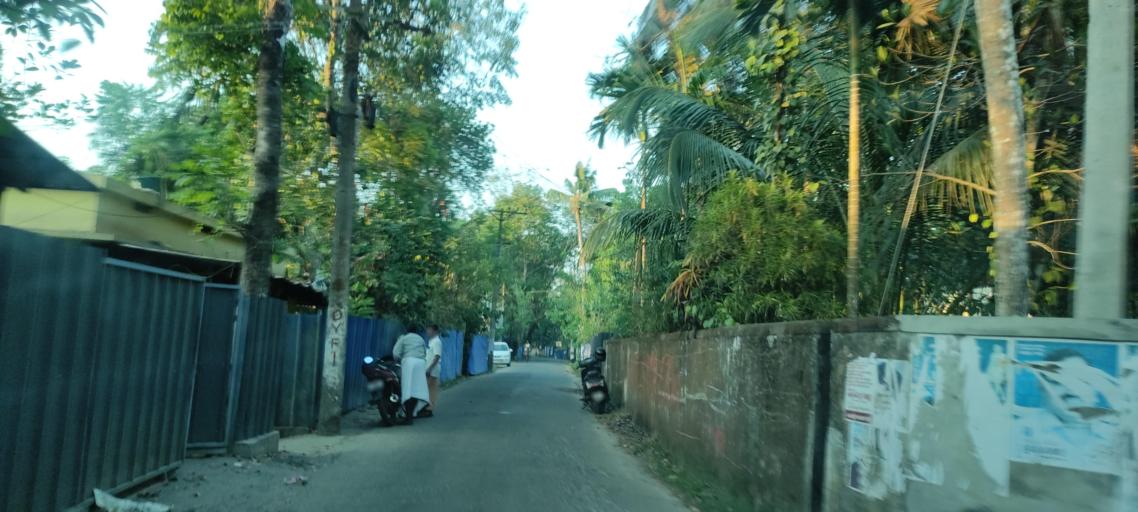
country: IN
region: Kerala
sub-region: Alappuzha
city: Kutiatodu
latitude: 9.7854
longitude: 76.3240
